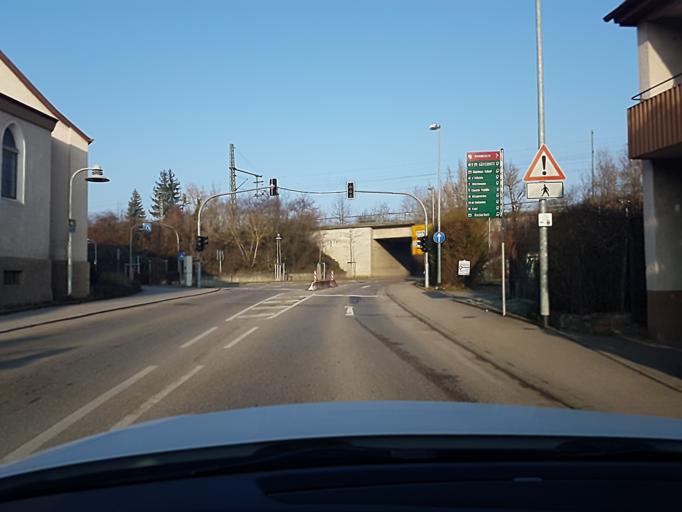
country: DE
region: Baden-Wuerttemberg
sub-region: Regierungsbezirk Stuttgart
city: Lauffen am Neckar
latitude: 49.0777
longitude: 9.1513
